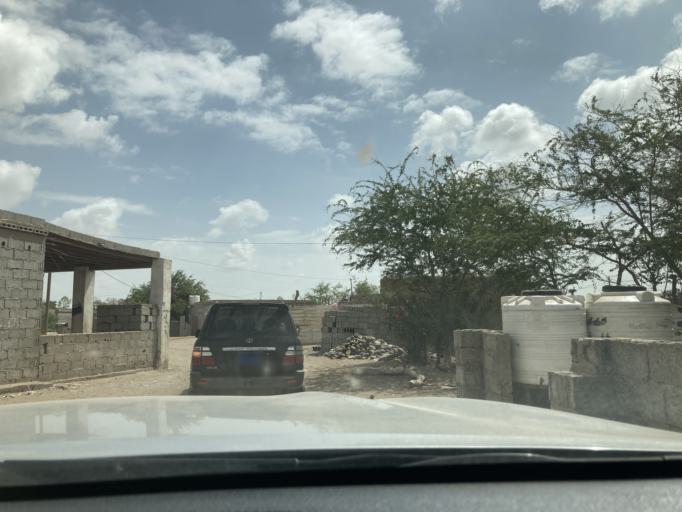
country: YE
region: Lahij
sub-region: Al  Hawtah
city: Lahij
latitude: 13.0165
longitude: 45.0049
